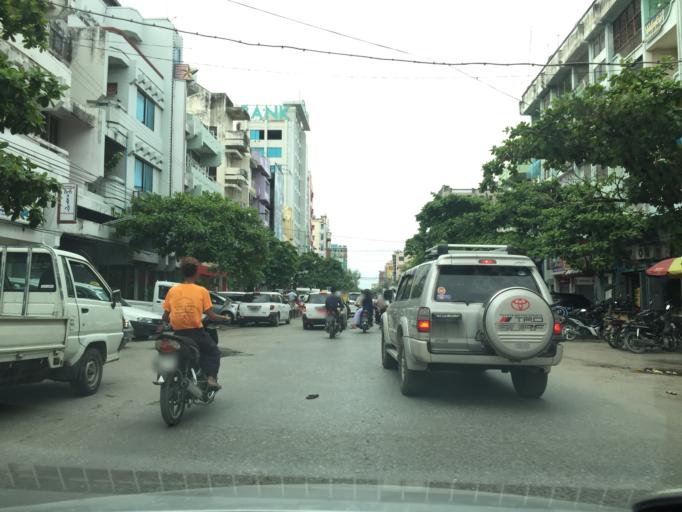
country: MM
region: Mandalay
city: Mandalay
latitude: 21.9815
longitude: 96.0811
